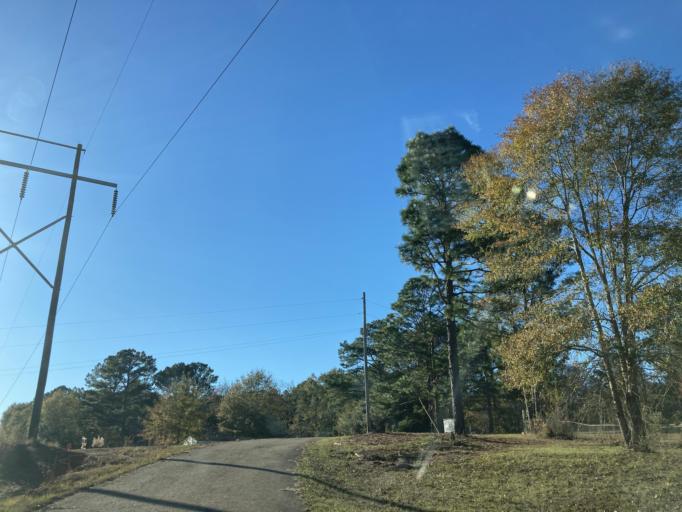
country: US
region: Mississippi
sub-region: Lamar County
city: Sumrall
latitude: 31.3891
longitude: -89.5649
